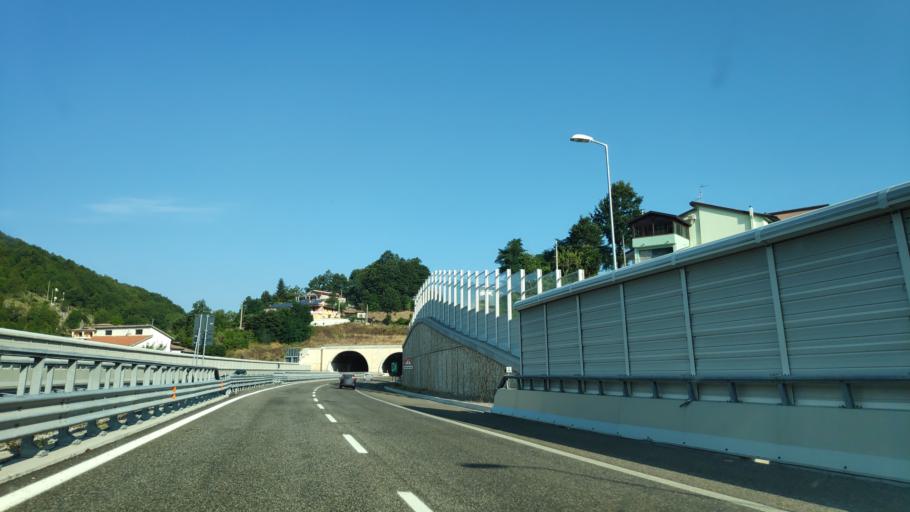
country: IT
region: Basilicate
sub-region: Provincia di Potenza
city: Lauria
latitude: 40.0204
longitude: 15.8823
